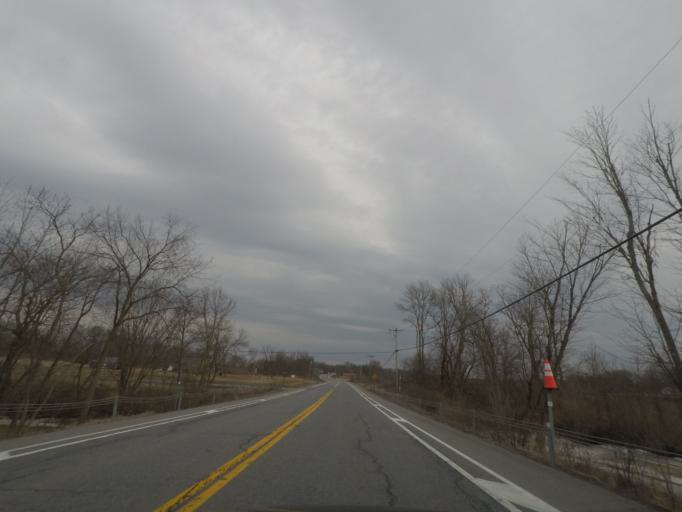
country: US
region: New York
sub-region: Washington County
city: Fort Edward
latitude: 43.2310
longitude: -73.5877
